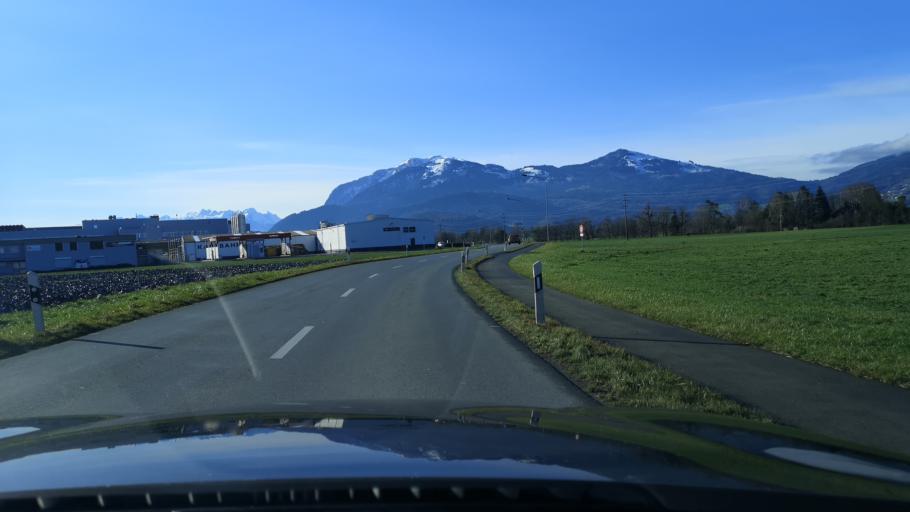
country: AT
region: Vorarlberg
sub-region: Politischer Bezirk Feldkirch
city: Koblach
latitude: 47.3507
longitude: 9.5930
